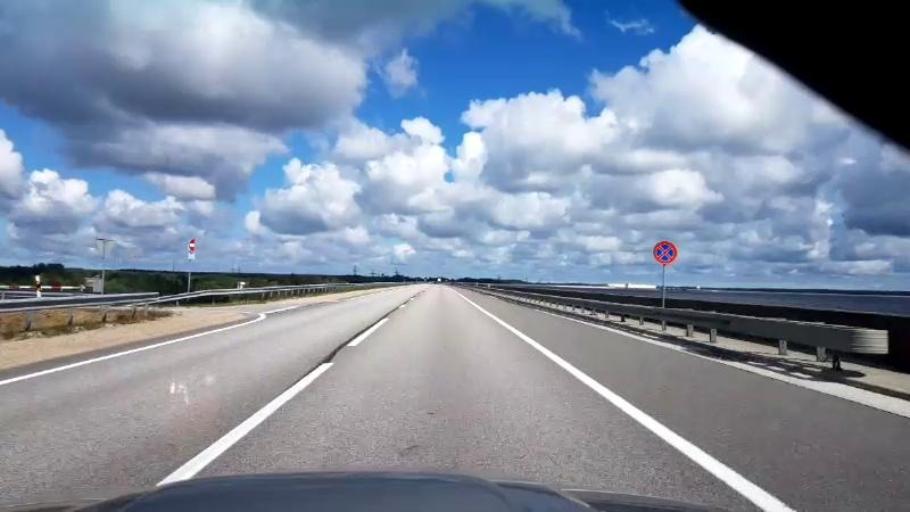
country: LV
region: Kekava
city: Kekava
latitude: 56.8306
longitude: 24.2720
